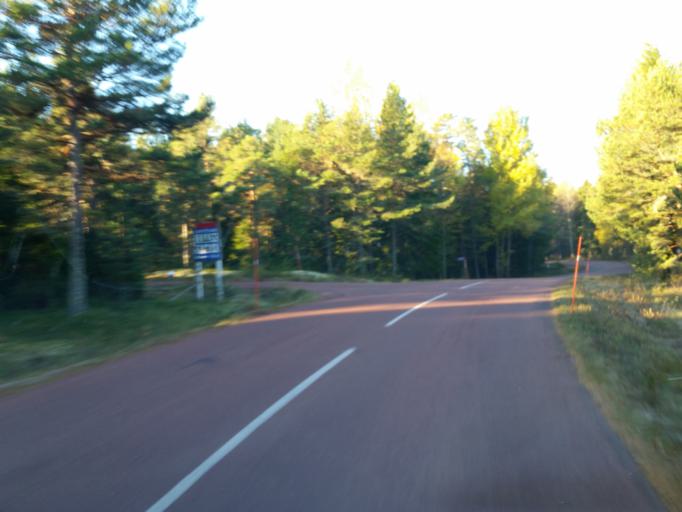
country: AX
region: Alands skaergard
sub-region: Vardoe
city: Vardoe
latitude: 60.2710
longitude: 20.3890
